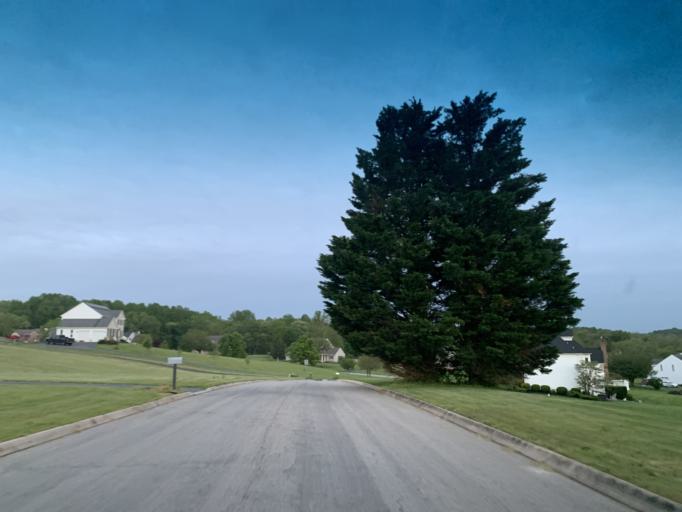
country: US
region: Maryland
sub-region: Harford County
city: South Bel Air
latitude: 39.5913
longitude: -76.2686
